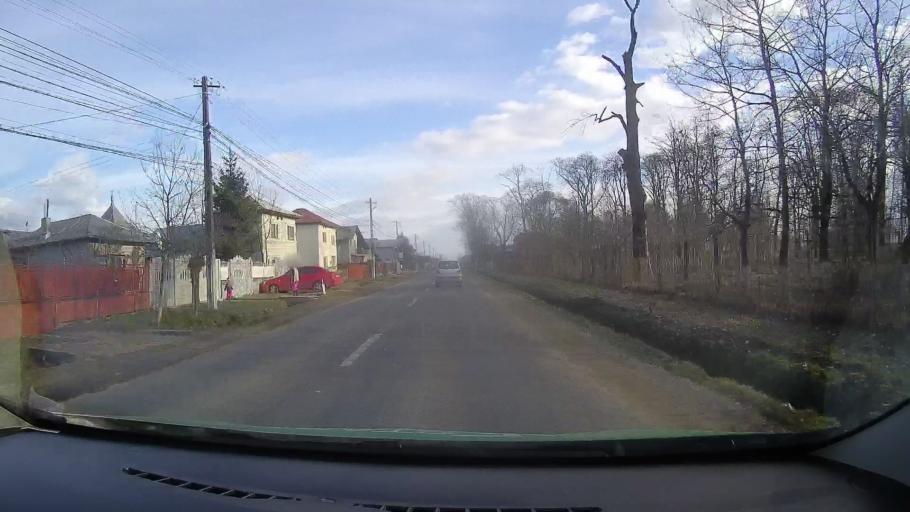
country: RO
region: Dambovita
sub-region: Comuna Vacaresti
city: Vacaresti
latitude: 44.8589
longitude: 25.4822
